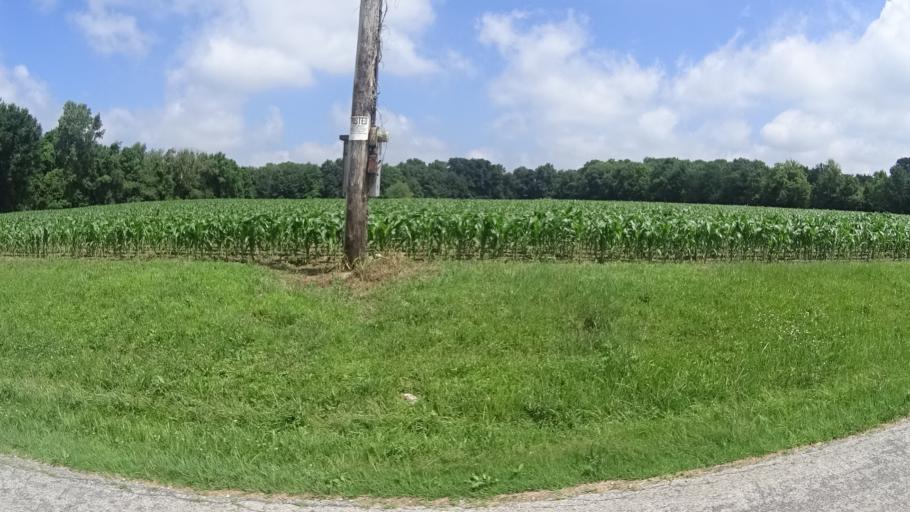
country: US
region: Ohio
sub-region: Huron County
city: Wakeman
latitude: 41.2985
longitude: -82.3501
